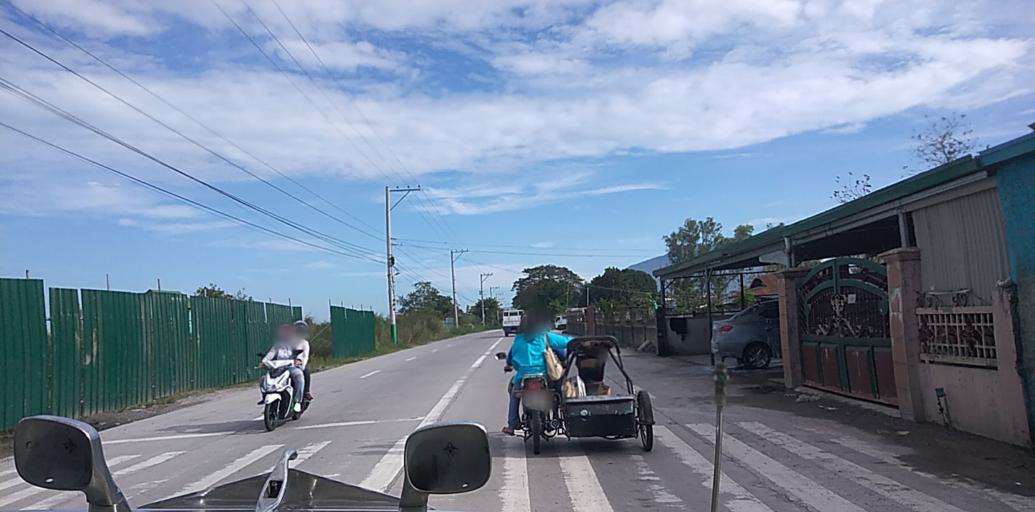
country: PH
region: Central Luzon
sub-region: Province of Pampanga
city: Malino
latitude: 15.1199
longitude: 120.6657
